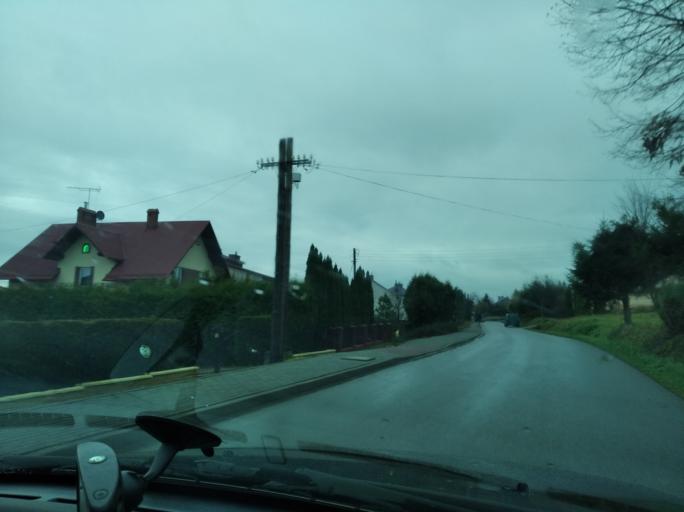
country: PL
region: Subcarpathian Voivodeship
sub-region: Powiat rzeszowski
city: Tyczyn
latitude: 49.9584
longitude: 22.0443
